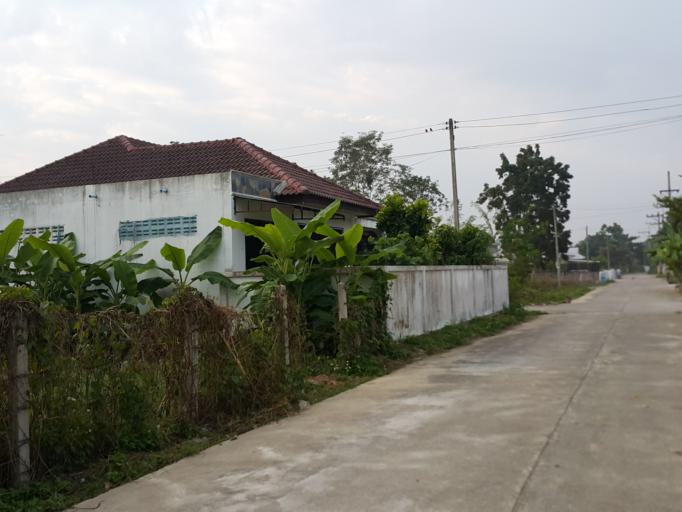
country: TH
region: Chiang Mai
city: San Kamphaeng
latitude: 18.7940
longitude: 99.1093
